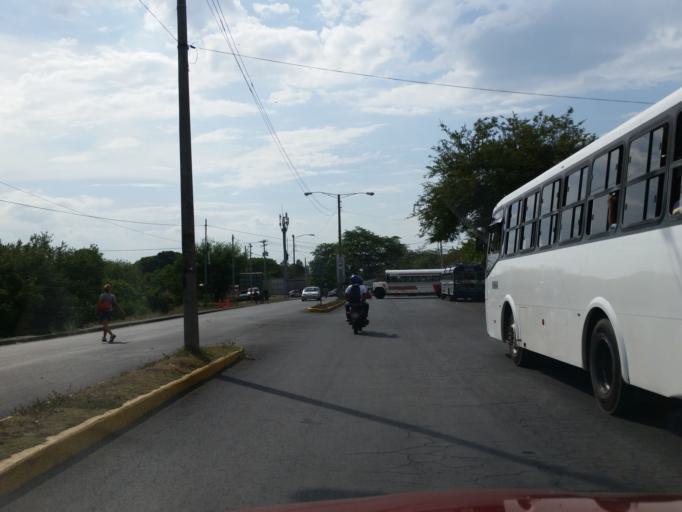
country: NI
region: Managua
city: Managua
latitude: 12.1234
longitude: -86.2452
